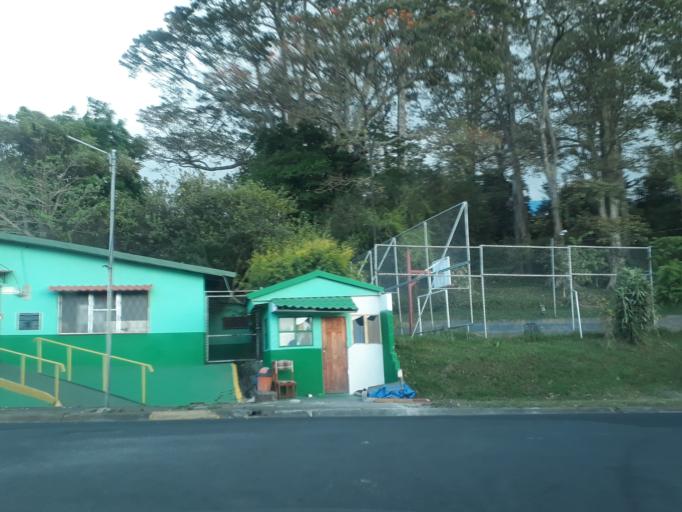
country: CR
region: San Jose
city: Purral
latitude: 9.9538
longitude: -84.0343
